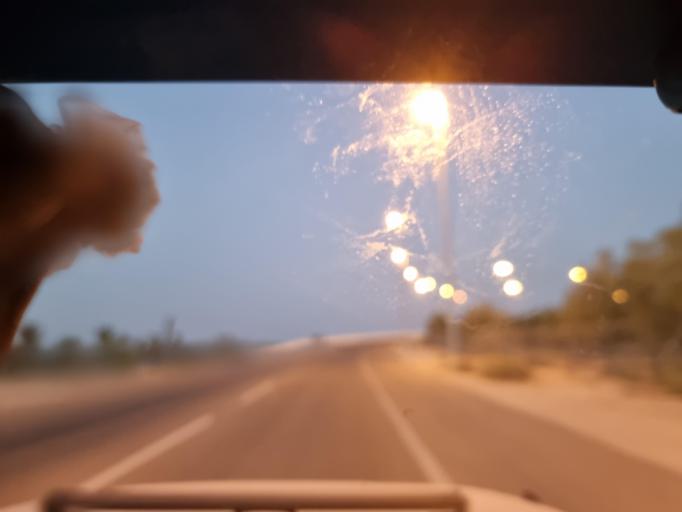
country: AE
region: Abu Dhabi
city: Abu Dhabi
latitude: 24.1915
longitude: 55.0001
